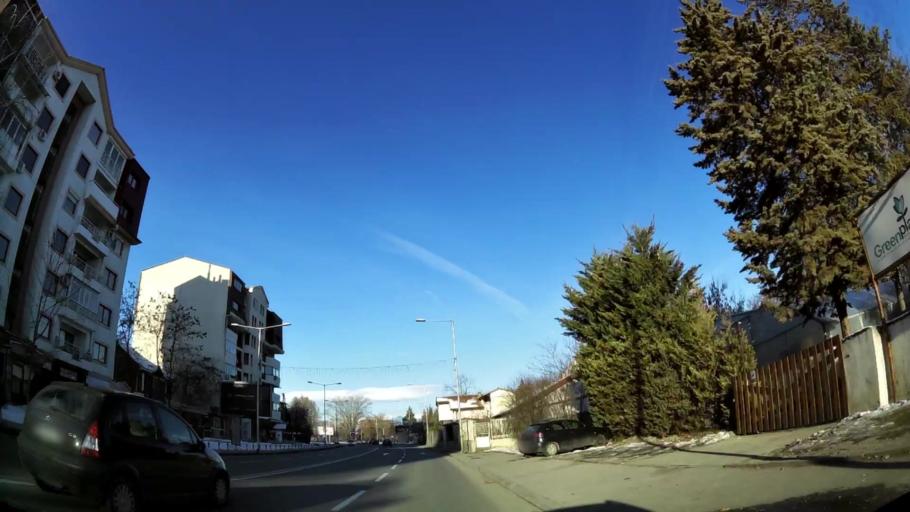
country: MK
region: Karpos
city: Skopje
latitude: 42.0062
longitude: 21.4156
